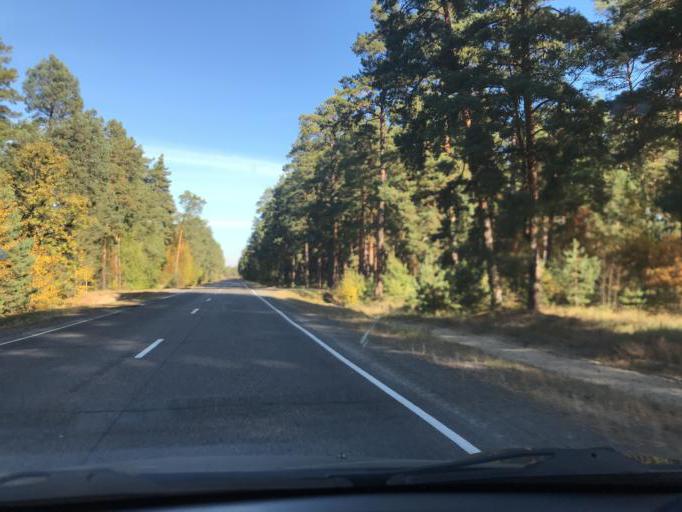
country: UA
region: Chernihiv
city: Lyubech
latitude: 51.5975
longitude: 30.4704
